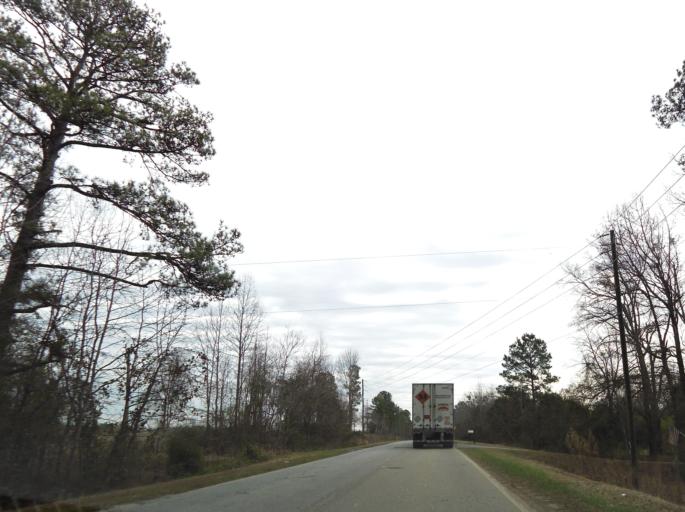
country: US
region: Georgia
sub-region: Houston County
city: Centerville
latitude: 32.6836
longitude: -83.6587
